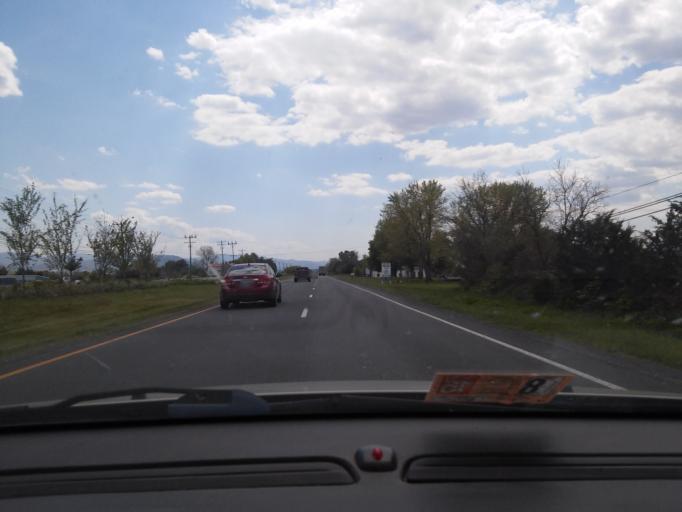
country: US
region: Virginia
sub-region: Warren County
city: Front Royal
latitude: 38.9982
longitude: -78.1745
